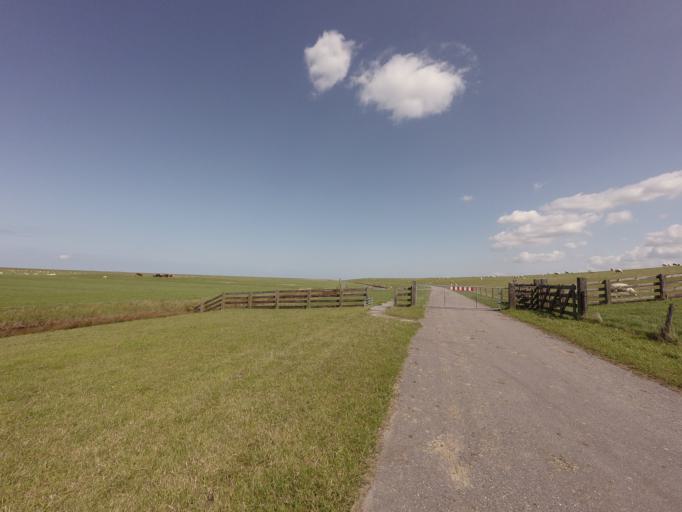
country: NL
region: Friesland
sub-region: Gemeente Ferwerderadiel
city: Marrum
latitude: 53.3336
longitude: 5.7790
